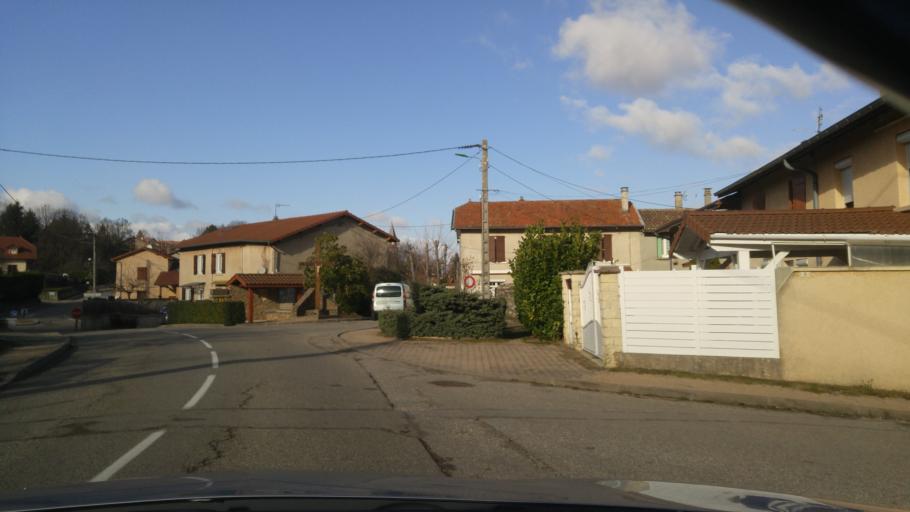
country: FR
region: Rhone-Alpes
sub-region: Departement de l'Isere
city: Roche
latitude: 45.5863
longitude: 5.1634
